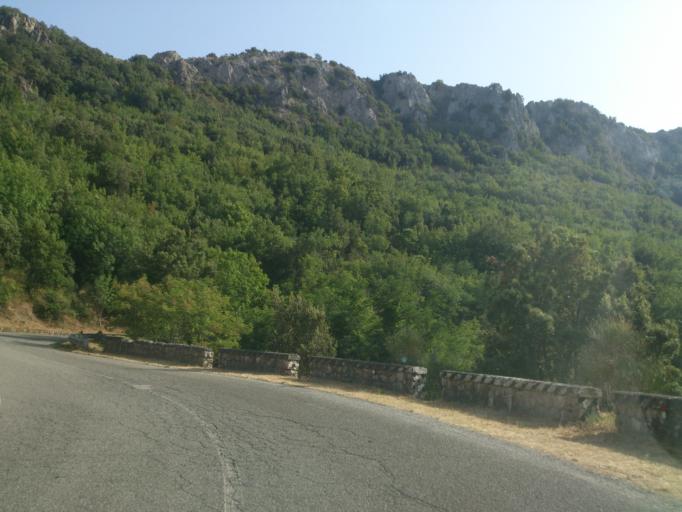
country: IT
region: Calabria
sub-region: Provincia di Reggio Calabria
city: Pazzano
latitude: 38.4671
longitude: 16.4359
